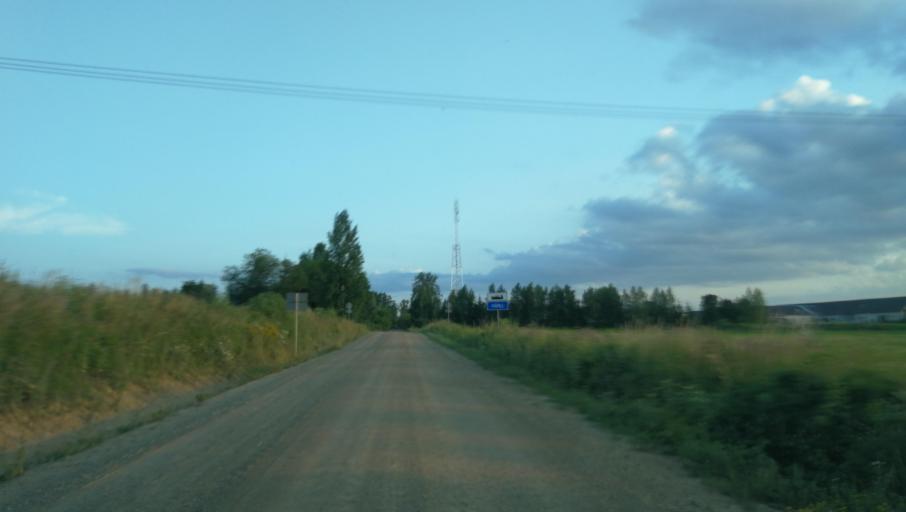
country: LV
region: Amatas Novads
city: Drabesi
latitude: 57.2501
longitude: 25.2162
